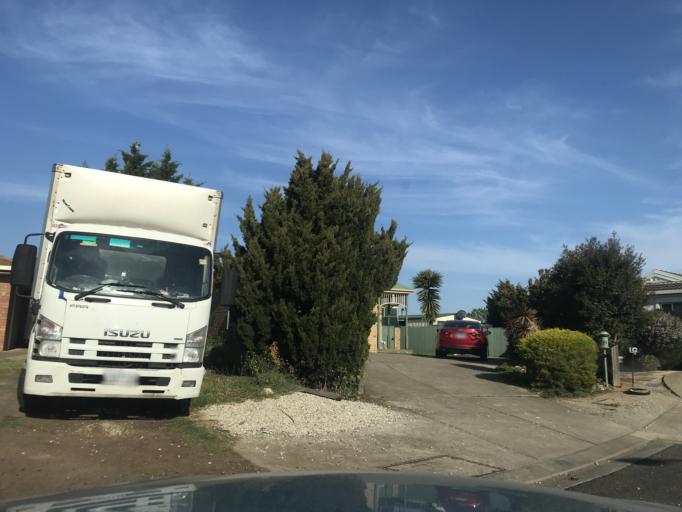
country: AU
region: Victoria
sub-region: Wyndham
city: Williams Landing
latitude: -37.8559
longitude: 144.7199
